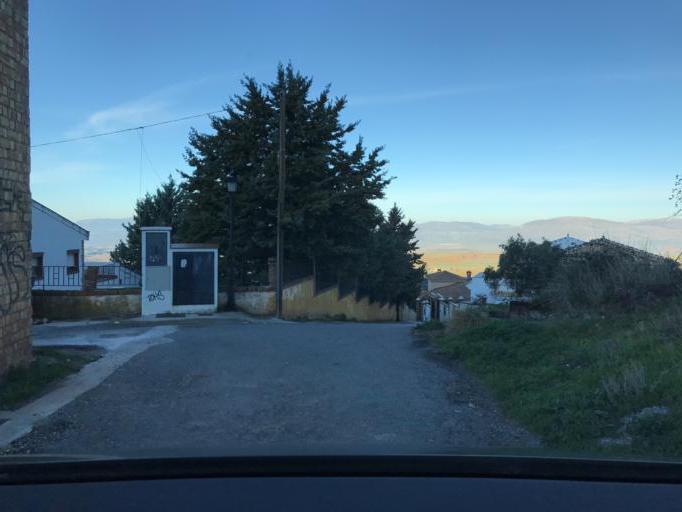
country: ES
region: Andalusia
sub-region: Provincia de Granada
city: Nivar
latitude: 37.2661
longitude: -3.5734
